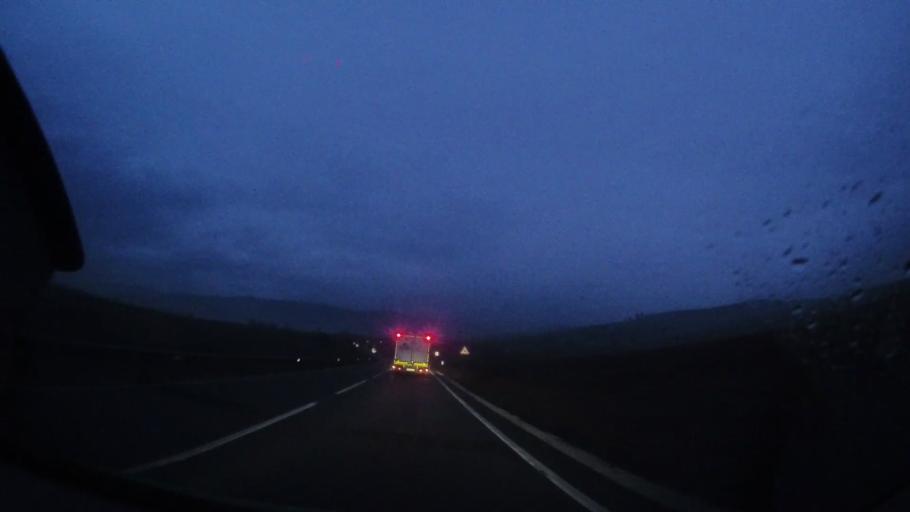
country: RO
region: Harghita
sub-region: Comuna Subcetate
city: Subcetate
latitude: 46.8538
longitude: 25.4692
